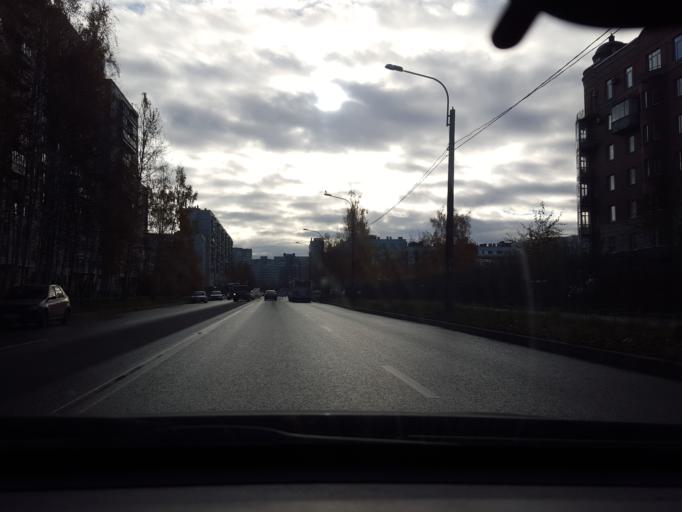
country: RU
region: St.-Petersburg
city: Ozerki
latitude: 60.0495
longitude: 30.3173
